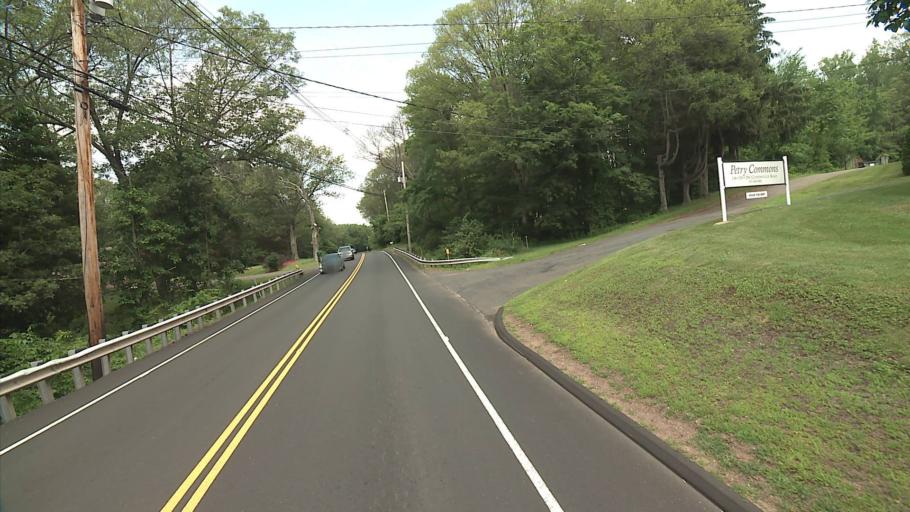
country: US
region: Connecticut
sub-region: New Haven County
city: Wallingford Center
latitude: 41.3945
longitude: -72.7944
